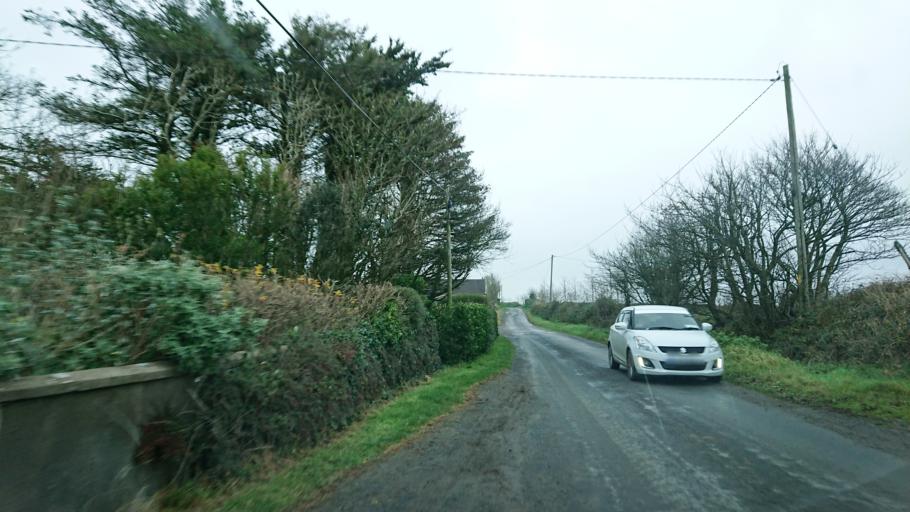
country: IE
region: Munster
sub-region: Waterford
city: Dunmore East
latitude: 52.1689
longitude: -7.0212
